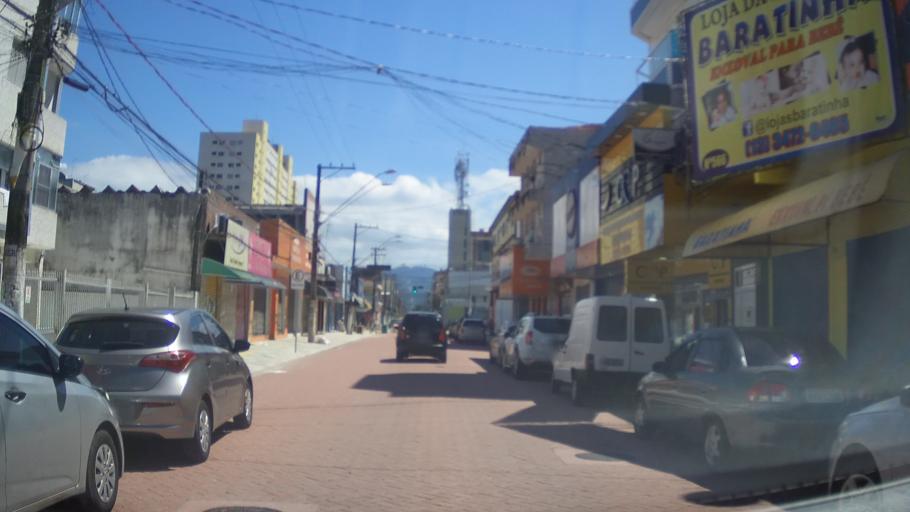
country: BR
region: Sao Paulo
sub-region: Praia Grande
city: Praia Grande
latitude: -24.0261
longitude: -46.4772
